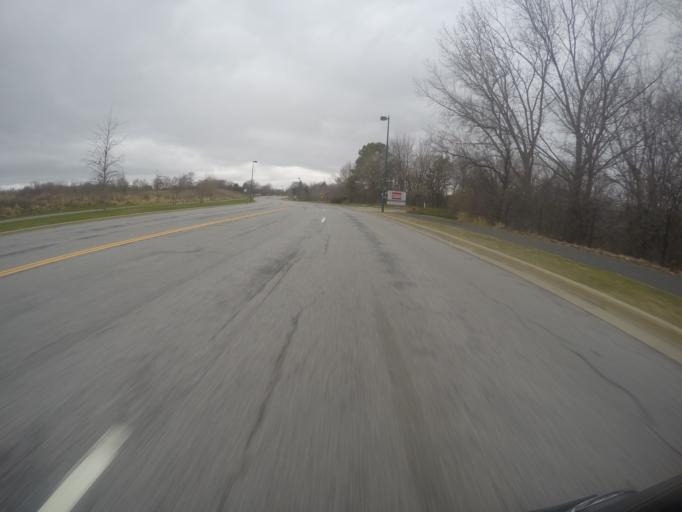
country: US
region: Minnesota
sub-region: Hennepin County
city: Eden Prairie
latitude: 44.8579
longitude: -93.4553
